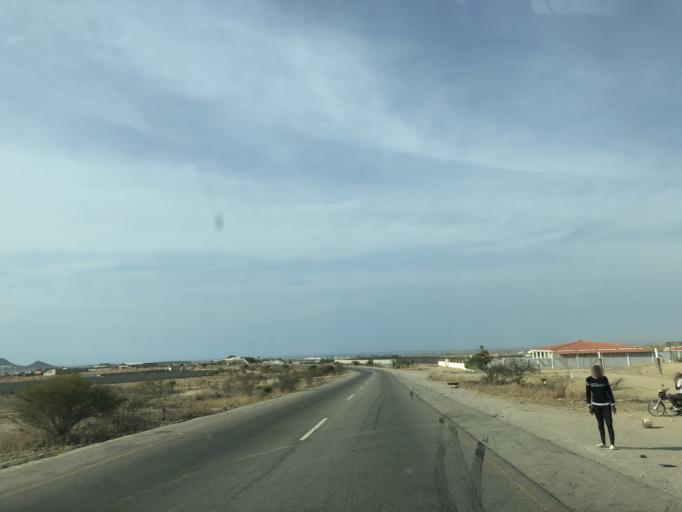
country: AO
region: Benguela
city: Benguela
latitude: -12.6973
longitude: 13.3449
